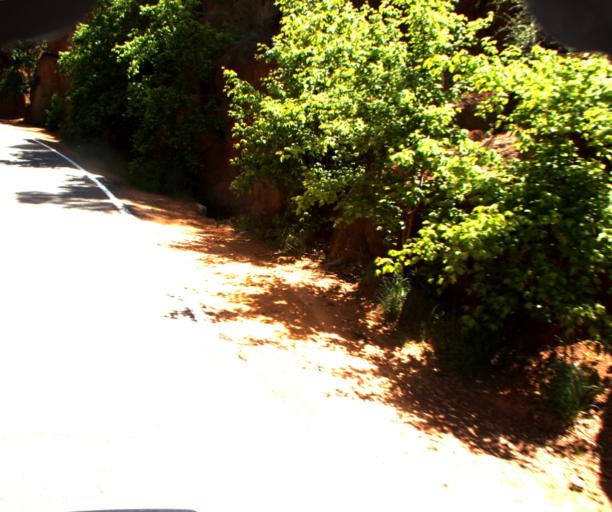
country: US
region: Arizona
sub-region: Coconino County
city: Sedona
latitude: 34.9288
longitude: -111.7397
